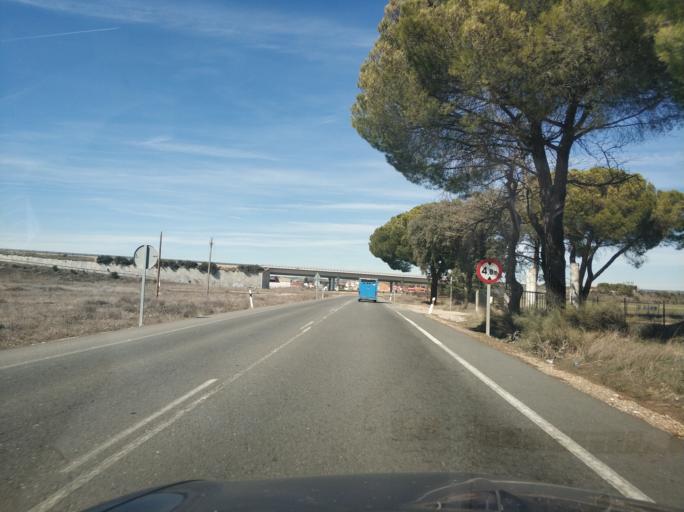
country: ES
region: Castille and Leon
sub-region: Provincia de Valladolid
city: Viana de Cega
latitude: 41.5474
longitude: -4.7857
